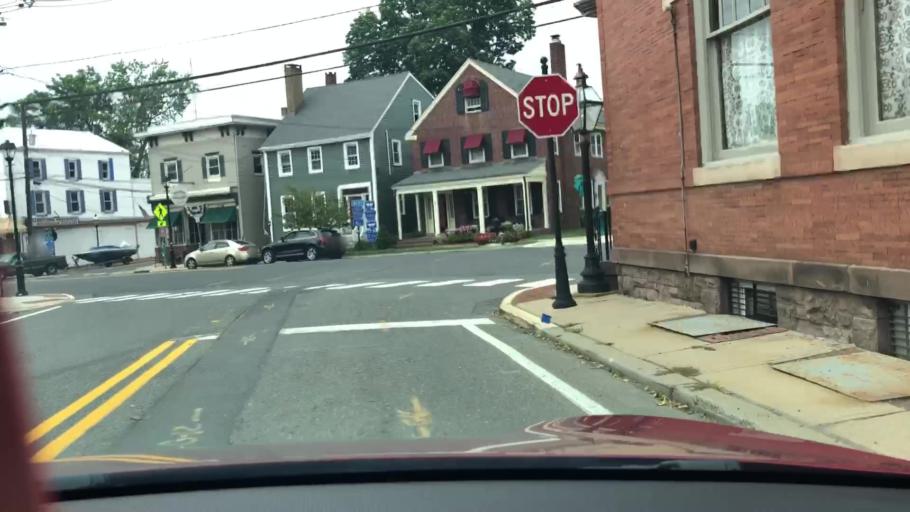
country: US
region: New Jersey
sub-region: Monmouth County
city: Allentown
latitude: 40.1779
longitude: -74.5838
